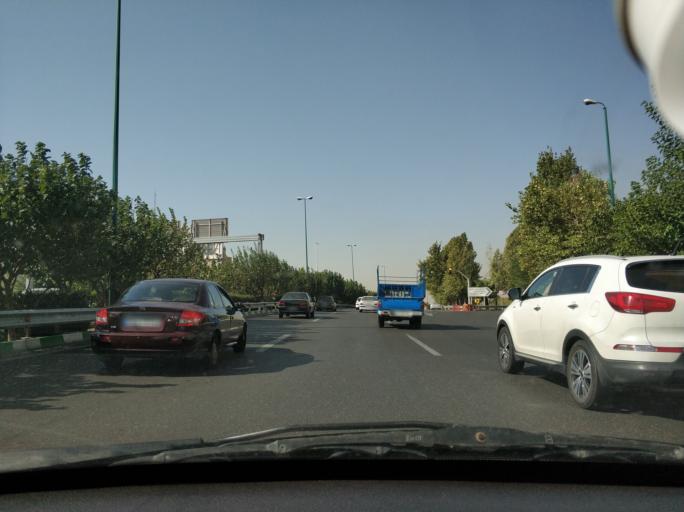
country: IR
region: Tehran
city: Tehran
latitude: 35.7420
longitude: 51.3991
